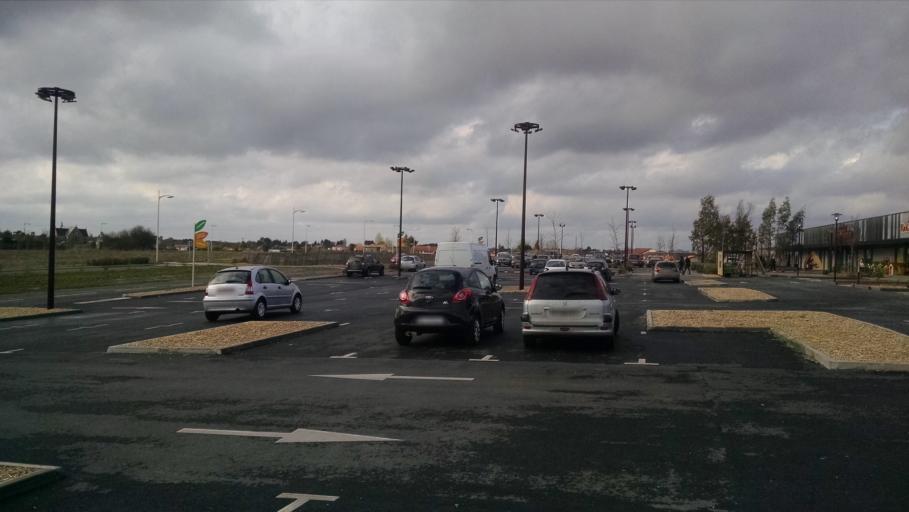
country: FR
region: Pays de la Loire
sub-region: Departement de la Loire-Atlantique
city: Getigne
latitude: 47.0859
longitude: -1.2621
